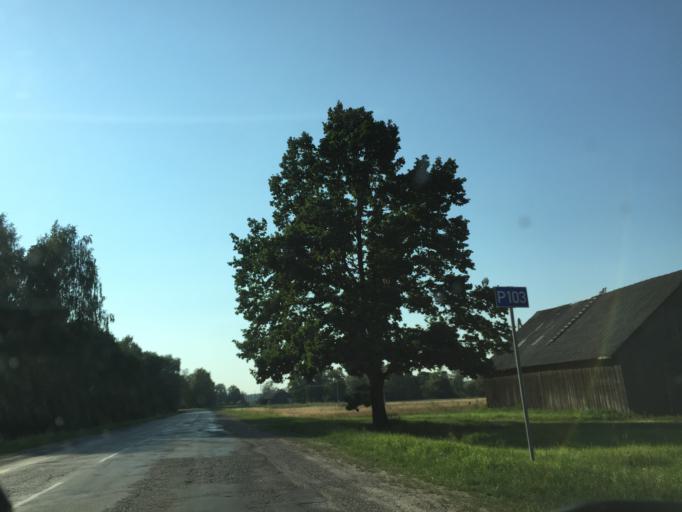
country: LV
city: Tervete
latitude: 56.4198
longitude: 23.5602
